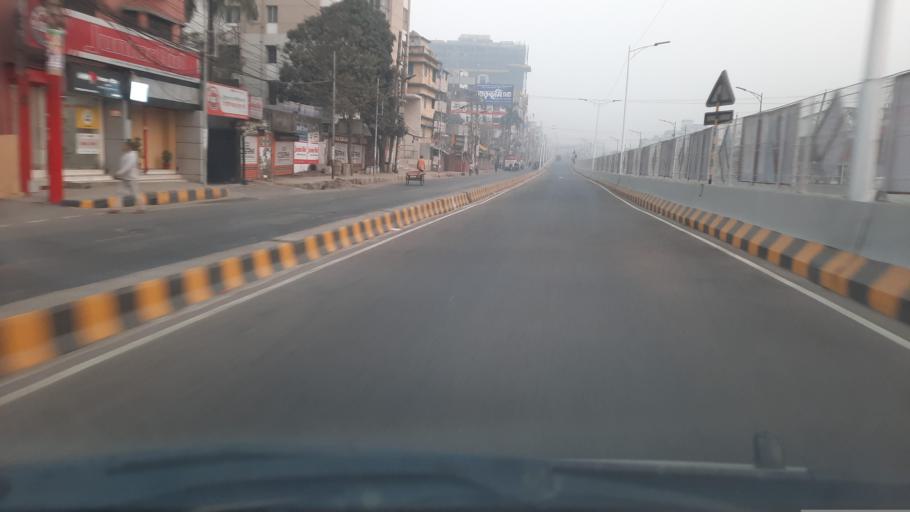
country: BD
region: Dhaka
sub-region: Dhaka
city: Dhaka
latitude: 23.7048
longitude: 90.4349
